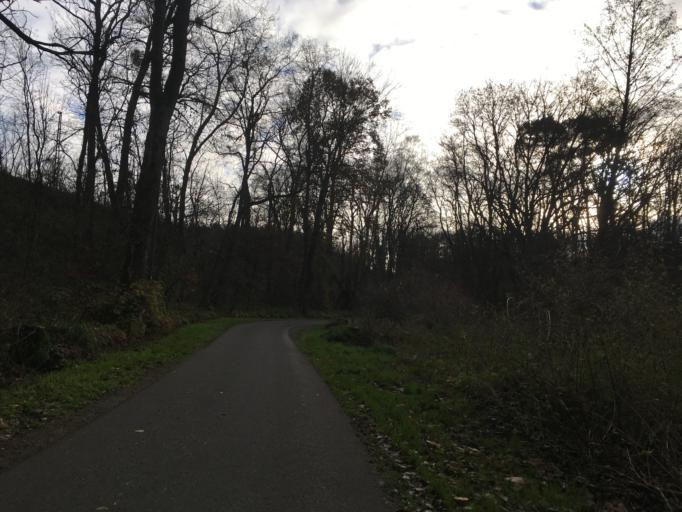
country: DE
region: Brandenburg
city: Buckow
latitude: 52.5549
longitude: 14.0794
